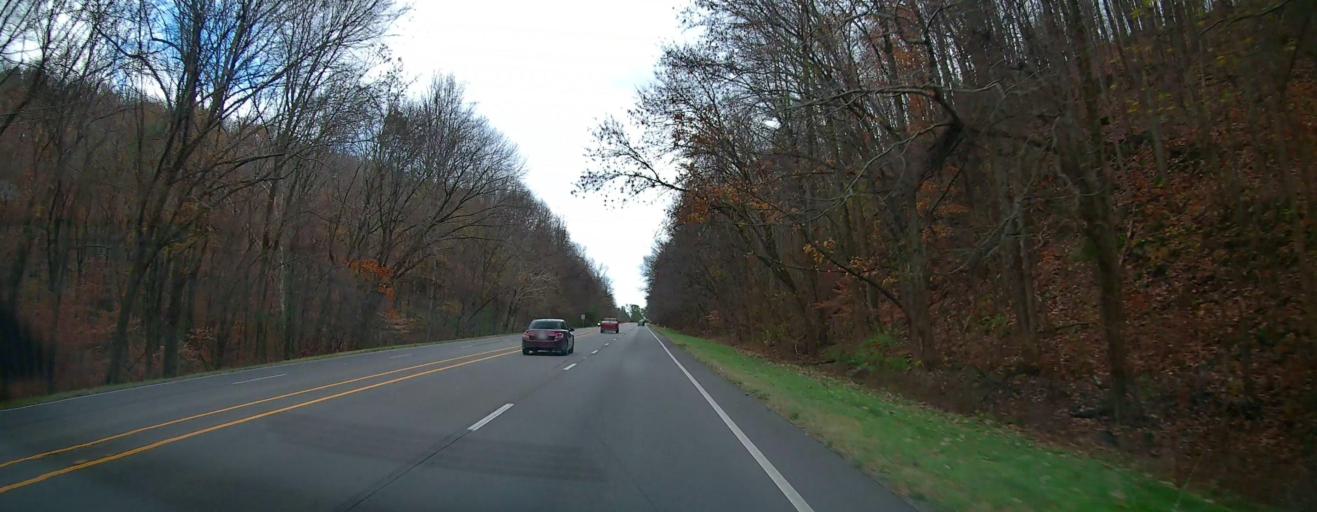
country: US
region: Alabama
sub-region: Morgan County
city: Falkville
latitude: 34.3137
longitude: -86.9988
